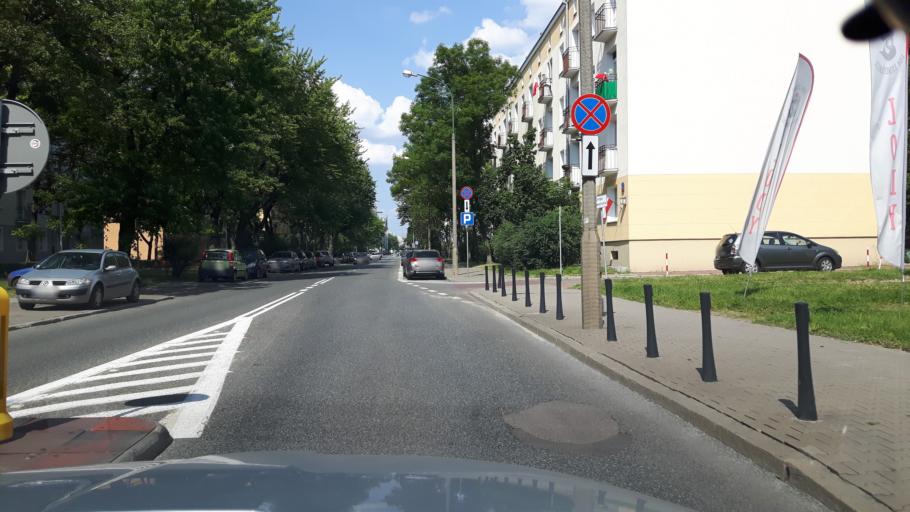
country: PL
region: Masovian Voivodeship
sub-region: Warszawa
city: Ochota
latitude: 52.2081
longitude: 20.9690
